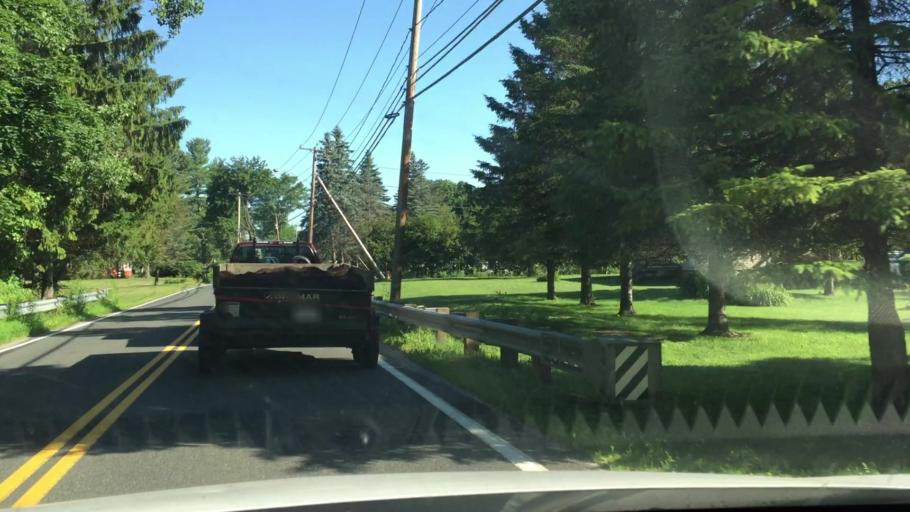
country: US
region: Massachusetts
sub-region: Berkshire County
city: Lee
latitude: 42.2909
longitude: -73.2380
